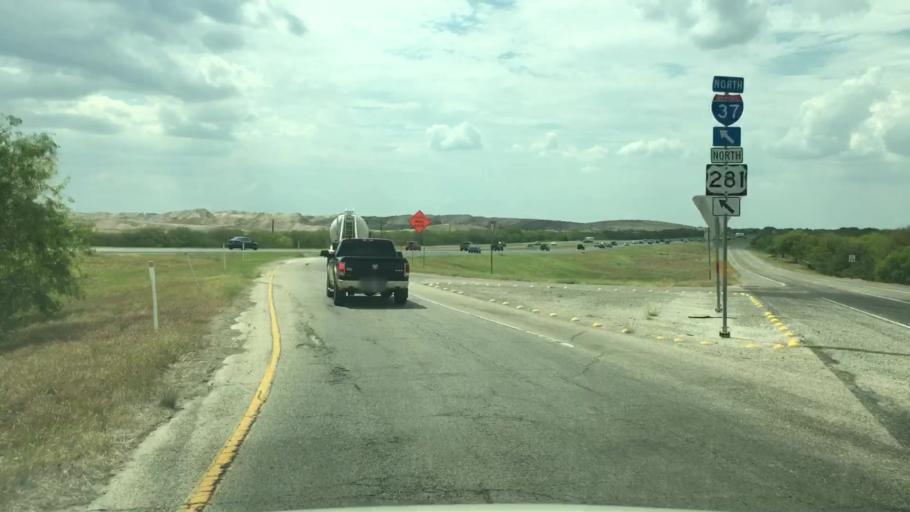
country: US
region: Texas
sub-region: Atascosa County
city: Pleasanton
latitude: 28.7866
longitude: -98.3231
